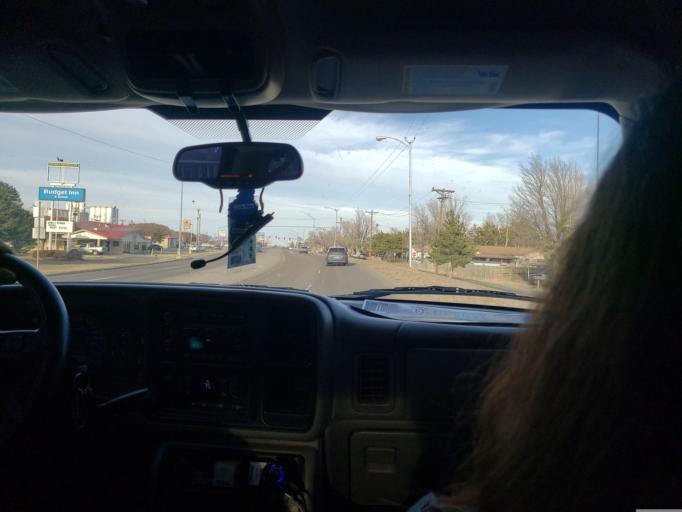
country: US
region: Oklahoma
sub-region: Texas County
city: Guymon
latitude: 36.6794
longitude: -101.4730
